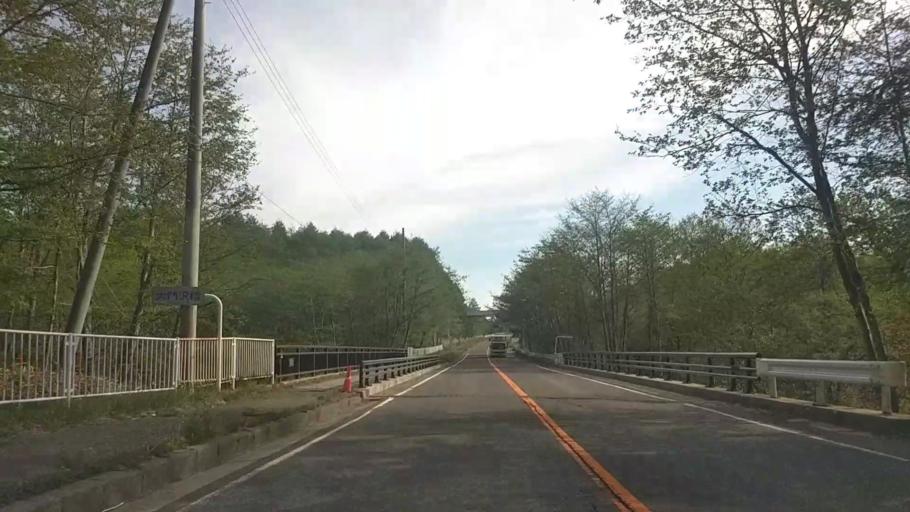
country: JP
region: Yamanashi
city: Nirasaki
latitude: 35.9397
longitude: 138.4493
